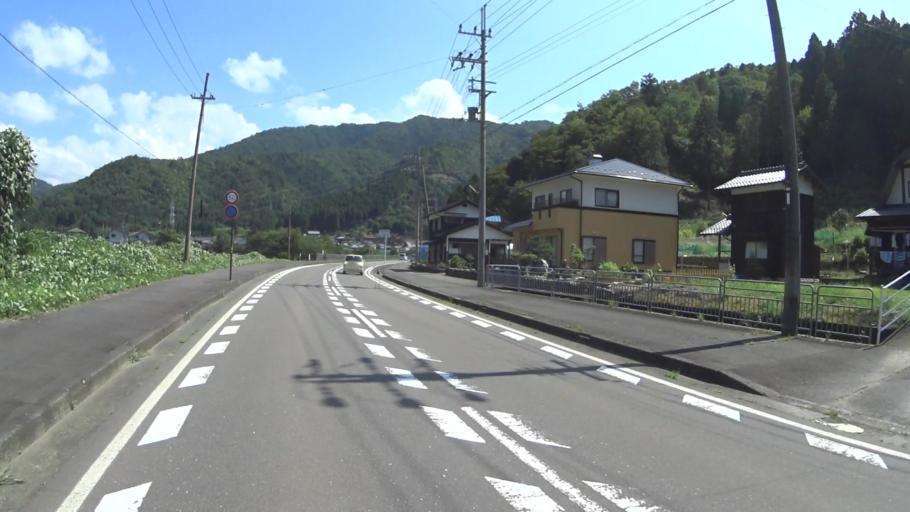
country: JP
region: Fukui
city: Obama
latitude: 35.4049
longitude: 135.6885
